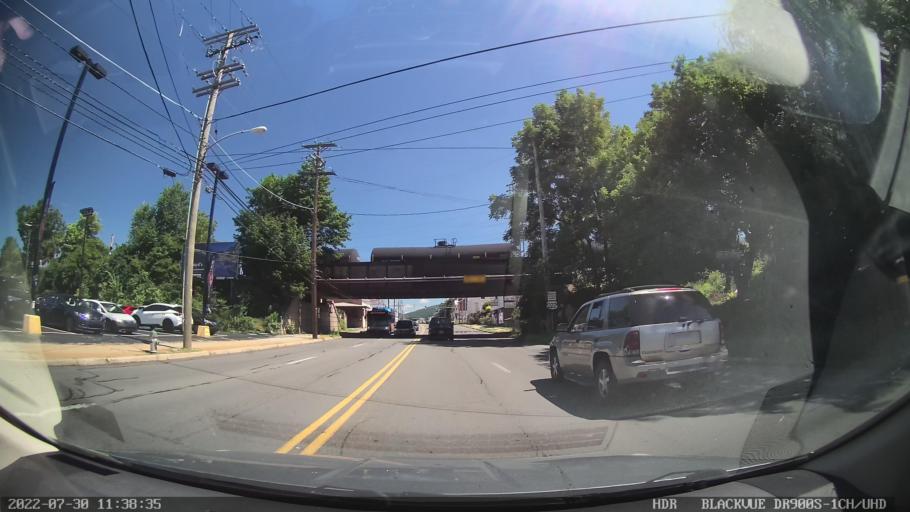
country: US
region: Pennsylvania
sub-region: Berks County
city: Kenhorst
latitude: 40.3164
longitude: -75.9387
